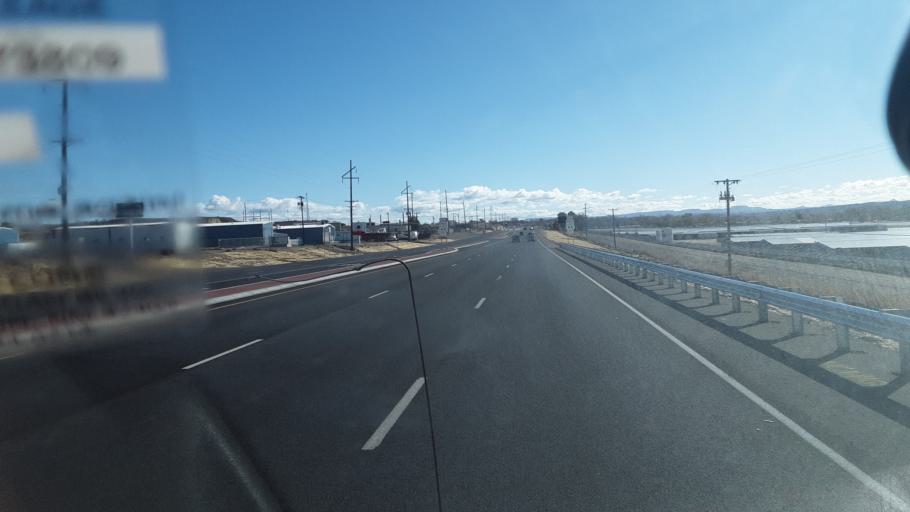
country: US
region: New Mexico
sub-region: San Juan County
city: Lee Acres
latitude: 36.7038
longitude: -108.1042
